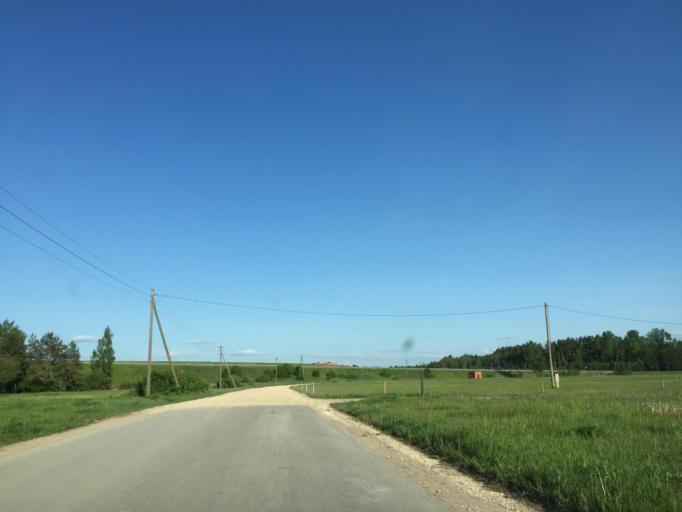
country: LV
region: Kekava
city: Kekava
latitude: 56.8251
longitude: 24.2707
